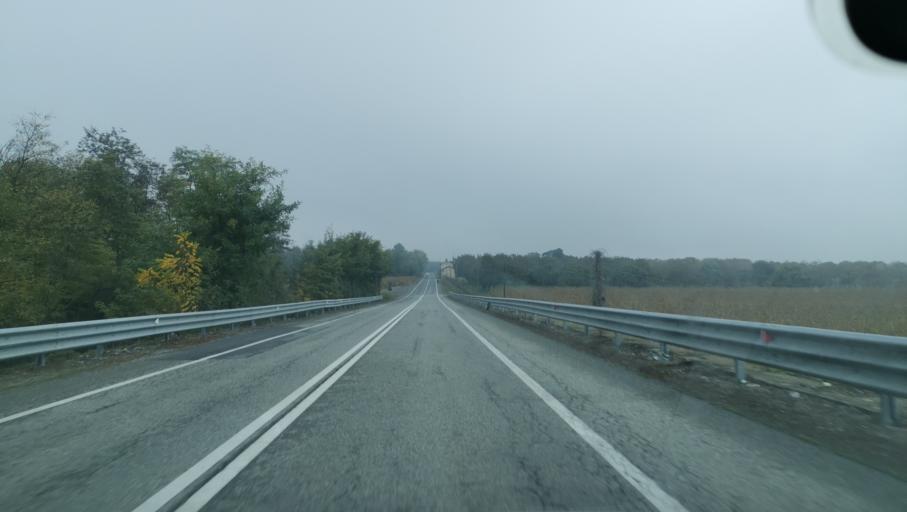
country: IT
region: Piedmont
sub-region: Provincia di Vercelli
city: Alice Castello
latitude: 45.3790
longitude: 8.0816
